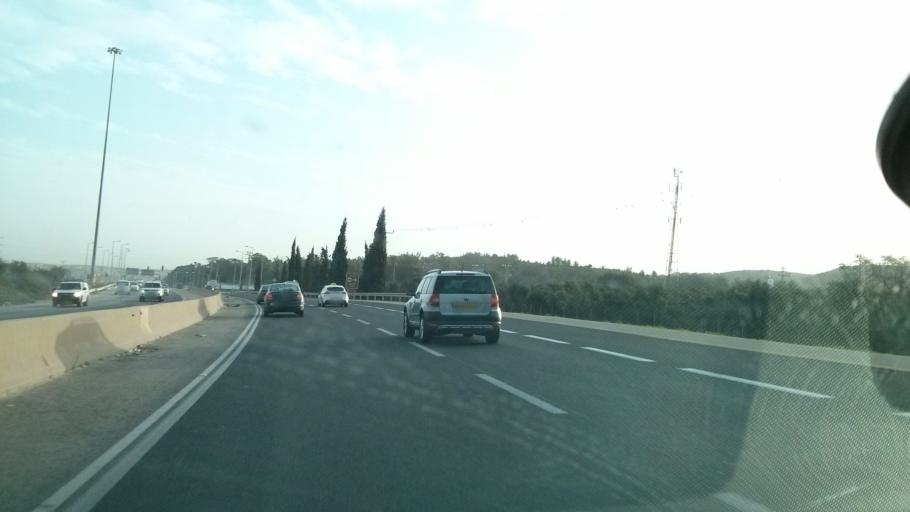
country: PS
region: West Bank
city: Barta`ah ash Sharqiyah
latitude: 32.4841
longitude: 35.0429
